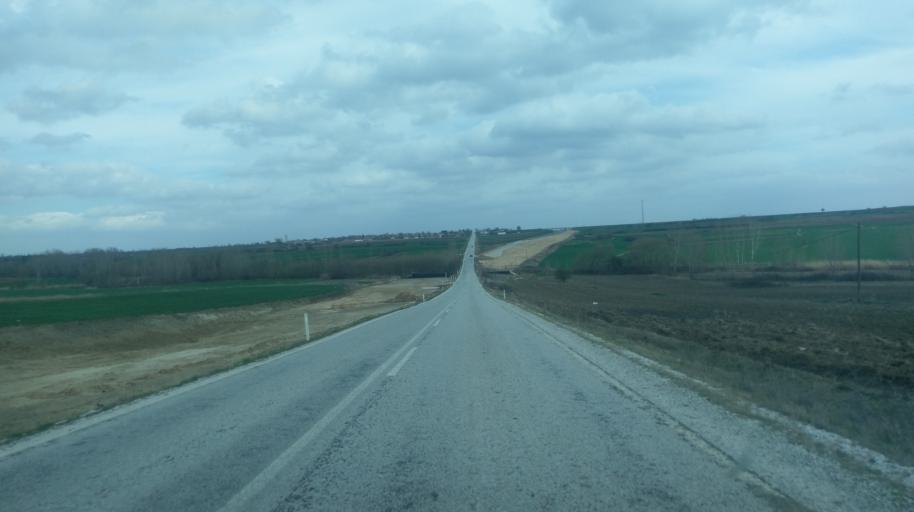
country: TR
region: Edirne
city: Haskoy
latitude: 41.6648
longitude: 26.9516
